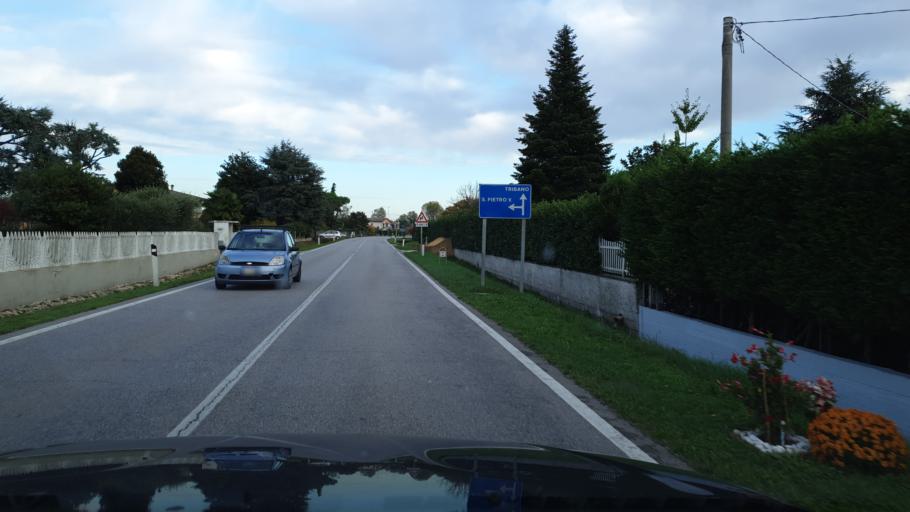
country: IT
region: Veneto
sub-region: Provincia di Padova
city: San Pietro Viminario
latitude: 45.2279
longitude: 11.8147
